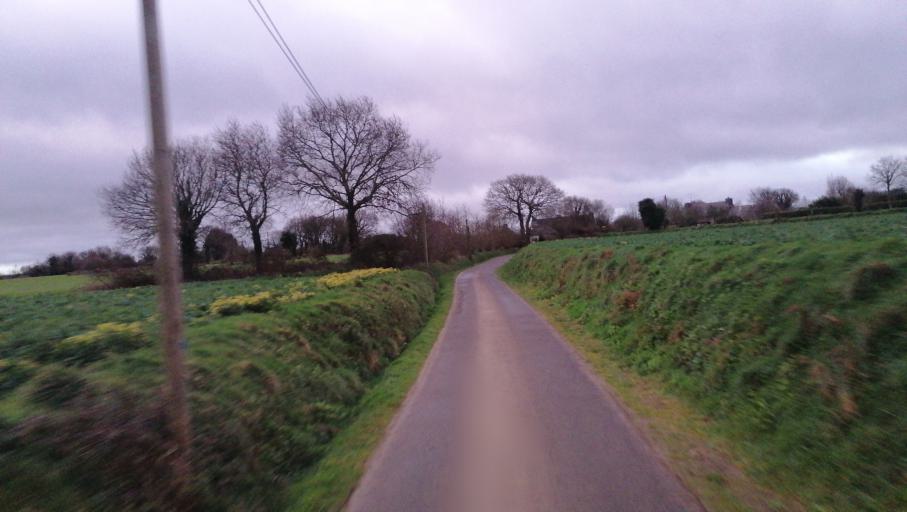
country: FR
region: Brittany
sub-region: Departement des Cotes-d'Armor
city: Plehedel
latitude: 48.6681
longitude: -3.0296
